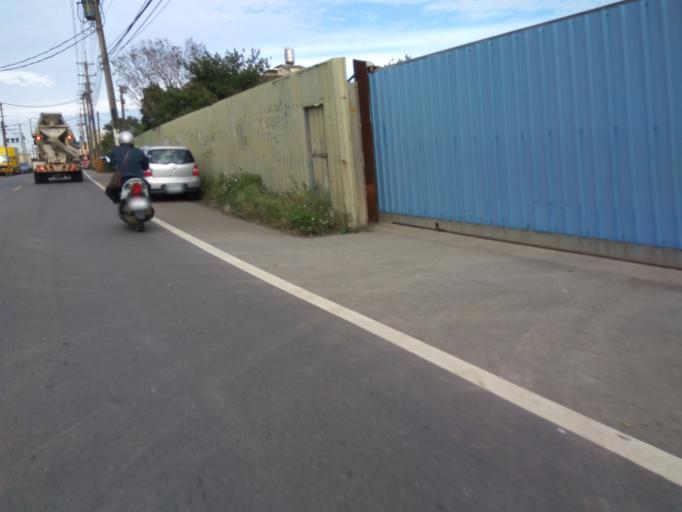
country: TW
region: Taiwan
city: Daxi
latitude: 24.9402
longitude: 121.1593
